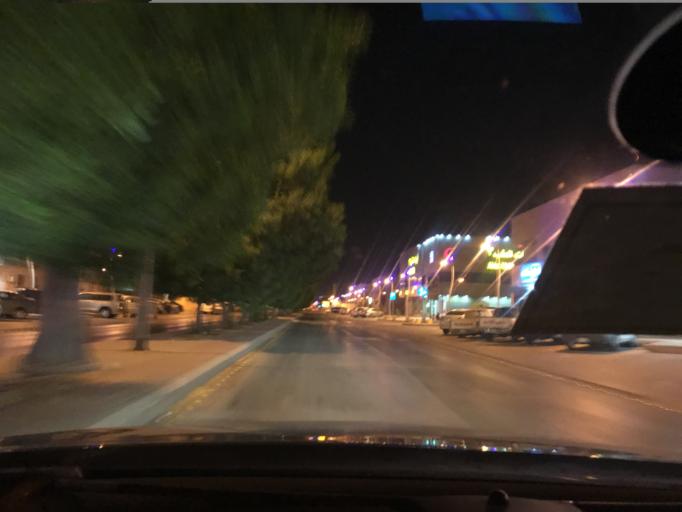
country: SA
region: Ar Riyad
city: Riyadh
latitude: 24.7483
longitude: 46.7980
